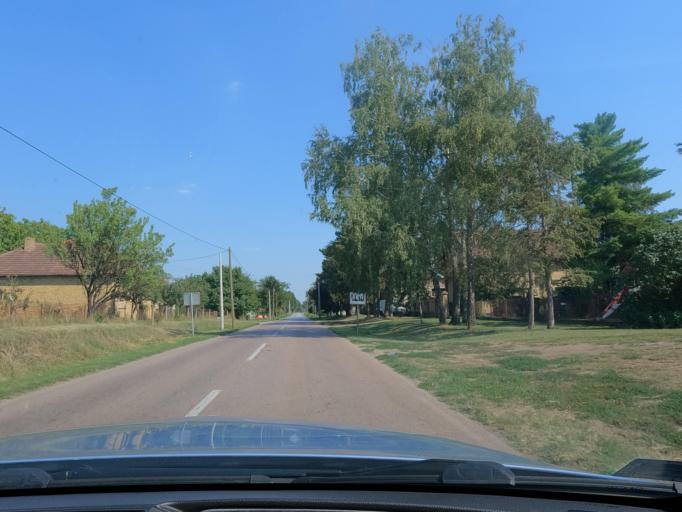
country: RS
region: Autonomna Pokrajina Vojvodina
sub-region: Severnobacki Okrug
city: Mali Igos
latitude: 45.7640
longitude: 19.7461
